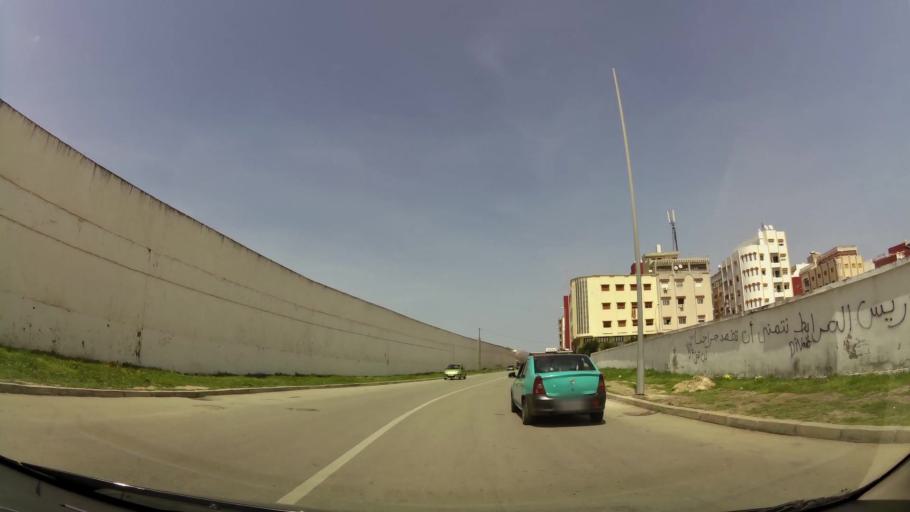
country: MA
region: Tanger-Tetouan
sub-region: Tanger-Assilah
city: Tangier
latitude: 35.7588
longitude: -5.8410
